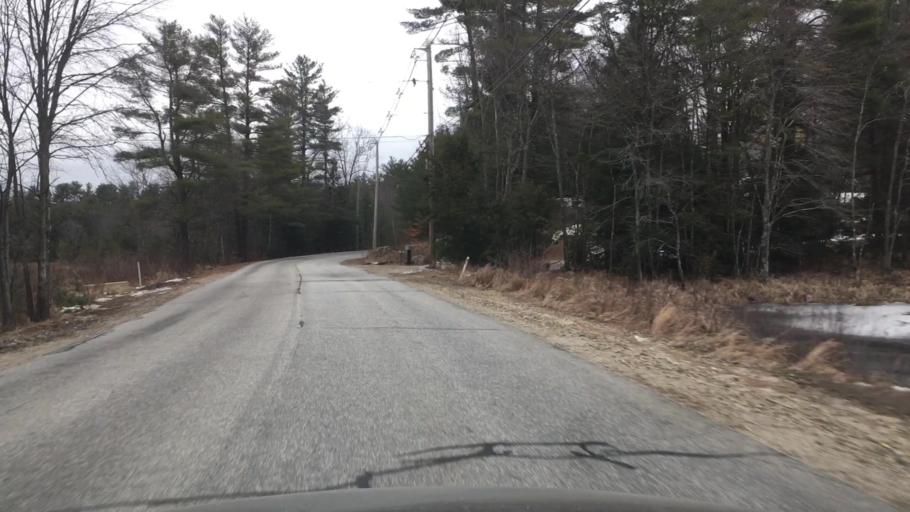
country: US
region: New Hampshire
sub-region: Hillsborough County
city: Goffstown
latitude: 42.9617
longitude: -71.6214
